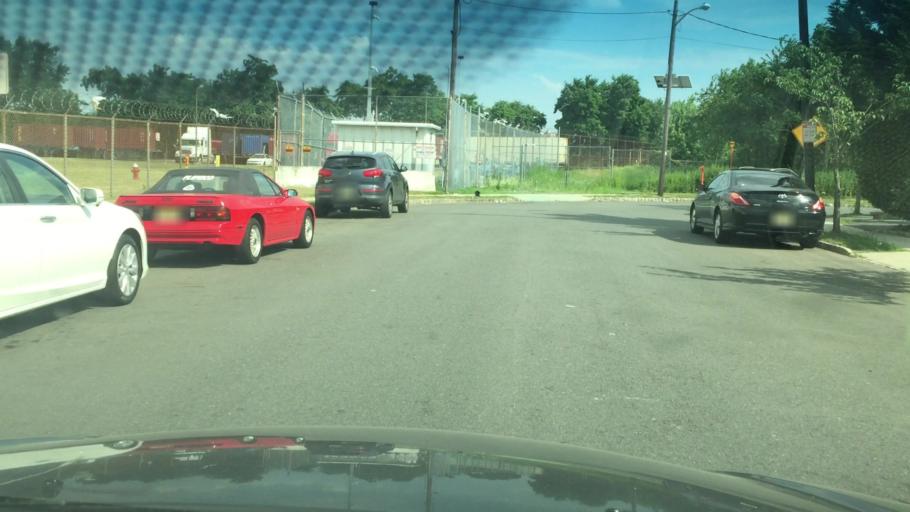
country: US
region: New Jersey
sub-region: Union County
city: Elizabeth
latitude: 40.6507
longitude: -74.1809
